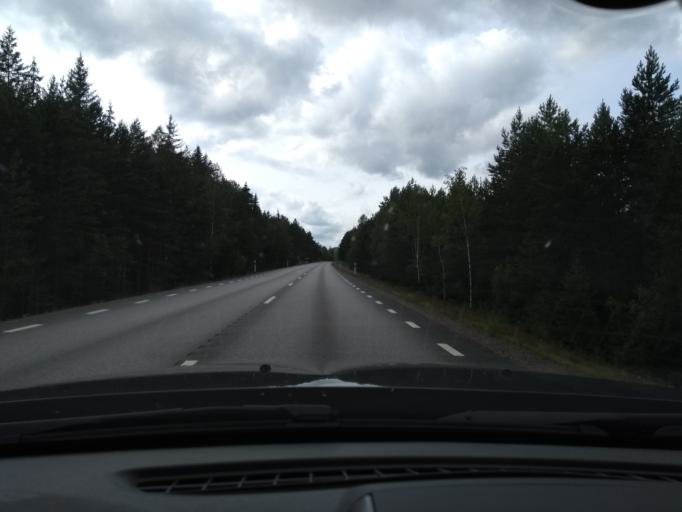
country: SE
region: Kalmar
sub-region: Vimmerby Kommun
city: Vimmerby
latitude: 57.6333
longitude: 15.7381
